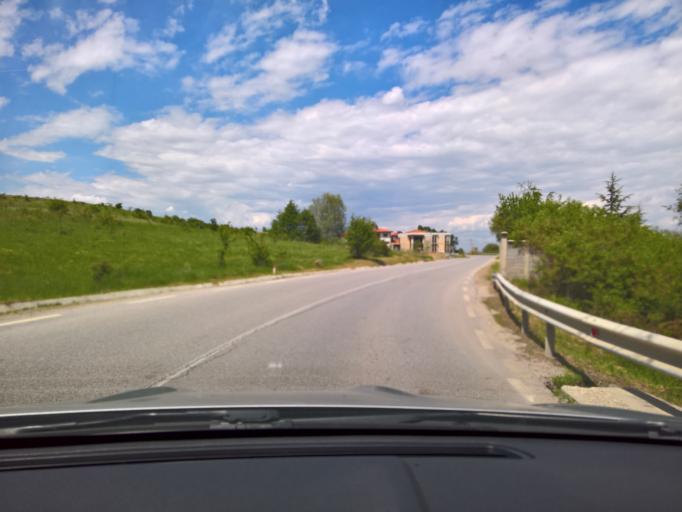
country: BG
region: Sofia-Capital
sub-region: Stolichna Obshtina
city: Sofia
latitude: 42.5745
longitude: 23.3589
